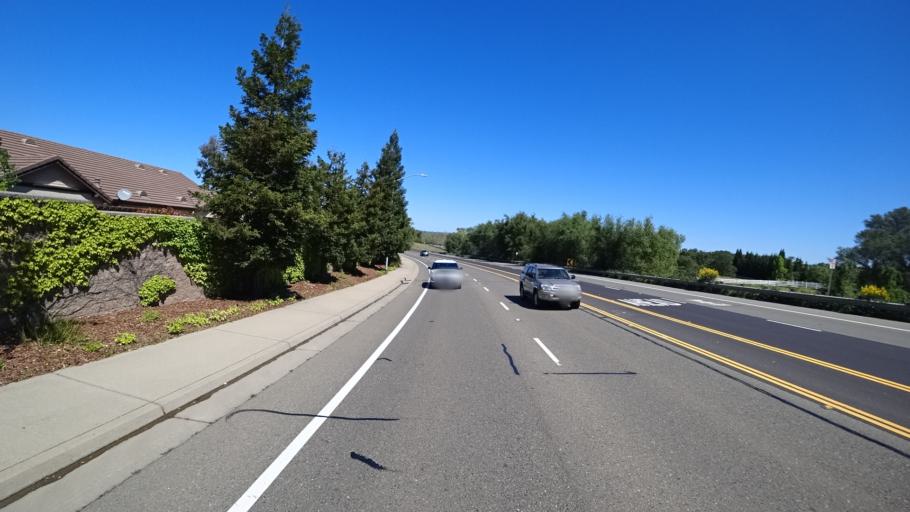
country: US
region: California
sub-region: Placer County
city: Rocklin
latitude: 38.7788
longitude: -121.2029
